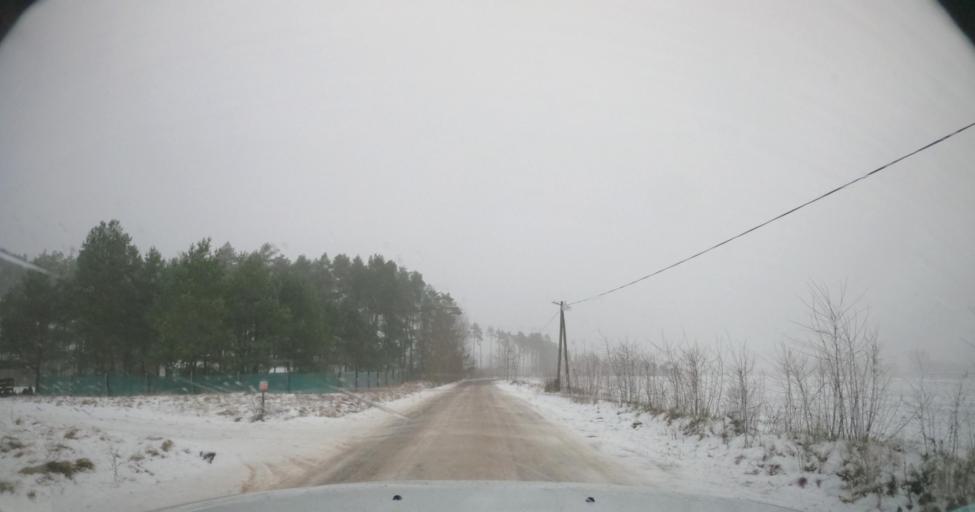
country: PL
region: West Pomeranian Voivodeship
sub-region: Powiat goleniowski
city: Przybiernow
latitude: 53.6872
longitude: 14.8450
